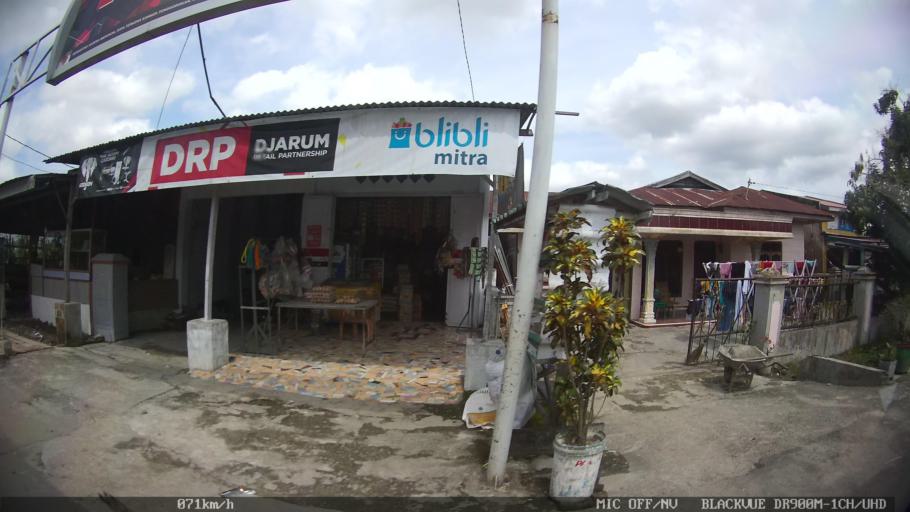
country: ID
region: North Sumatra
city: Percut
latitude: 3.5782
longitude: 98.8408
